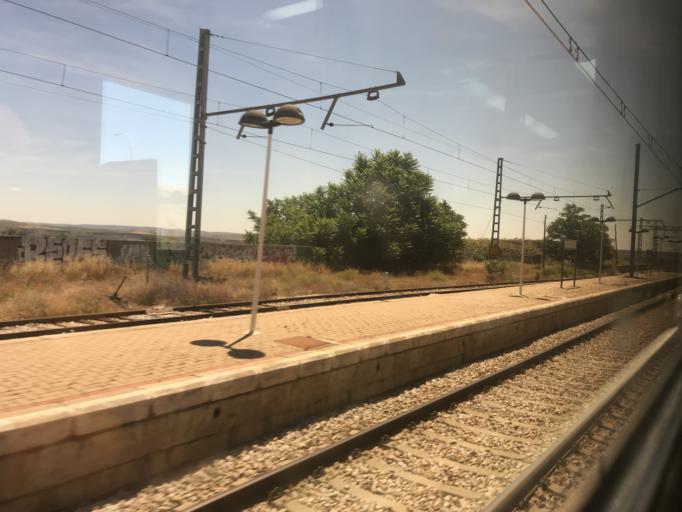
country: ES
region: Madrid
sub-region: Provincia de Madrid
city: Ciempozuelos
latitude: 40.1588
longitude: -3.6097
